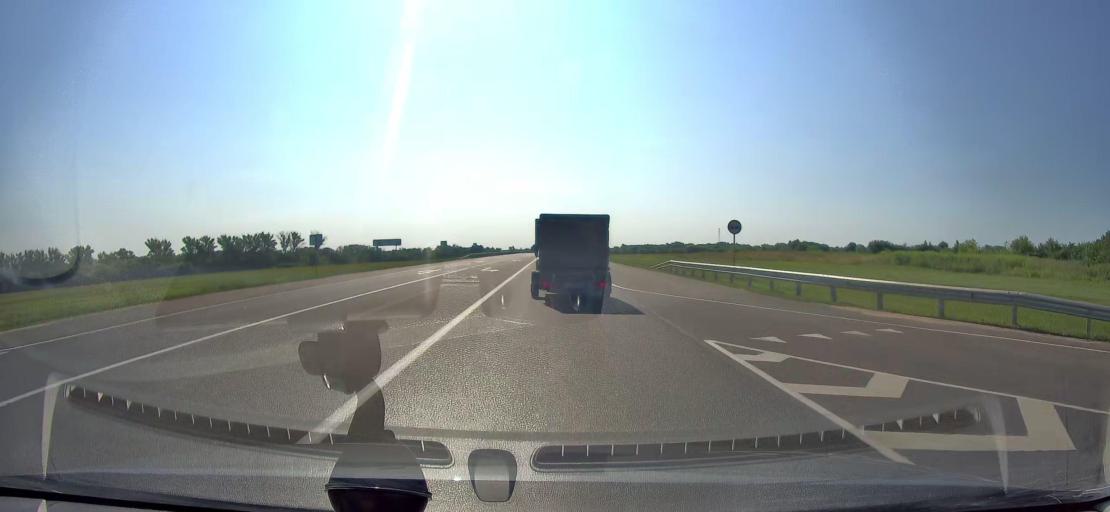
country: RU
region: Orjol
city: Kromy
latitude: 52.6497
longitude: 35.7364
